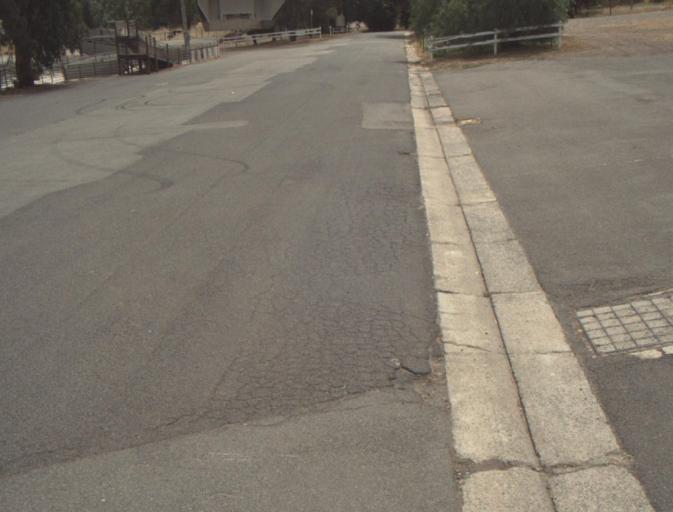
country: AU
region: Tasmania
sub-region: Launceston
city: Newstead
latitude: -41.4403
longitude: 147.1739
